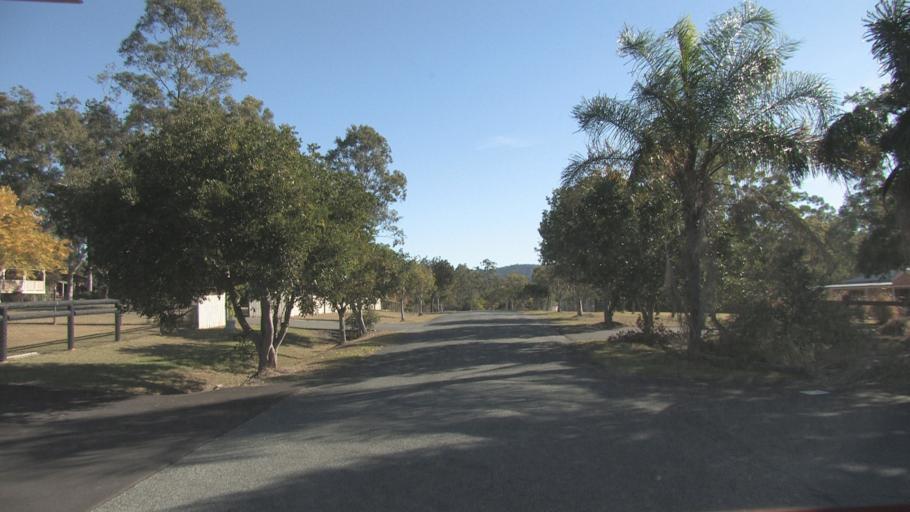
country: AU
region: Queensland
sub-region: Ipswich
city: Springfield Lakes
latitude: -27.7322
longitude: 152.9271
